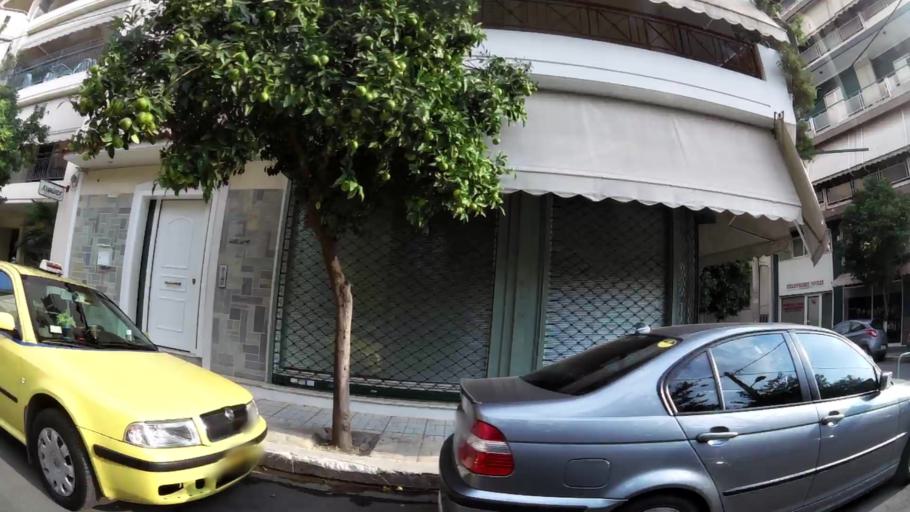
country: GR
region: Attica
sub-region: Nomarchia Athinas
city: Kallithea
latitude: 37.9501
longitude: 23.6950
